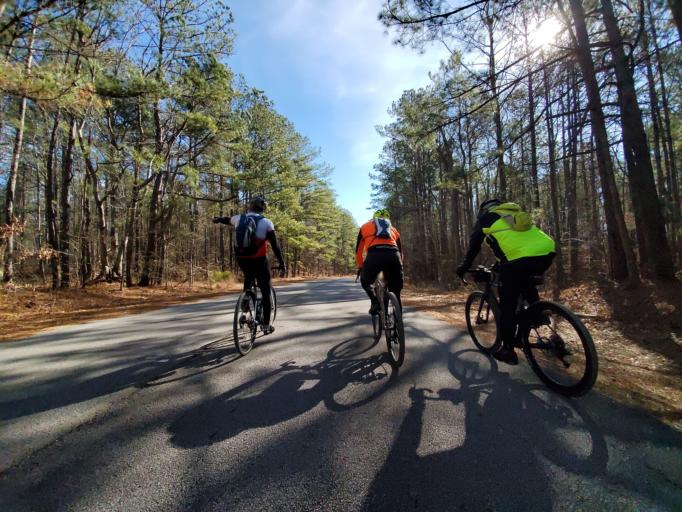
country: US
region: Georgia
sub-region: Fulton County
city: Chattahoochee Hills
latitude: 33.5739
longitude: -84.7746
